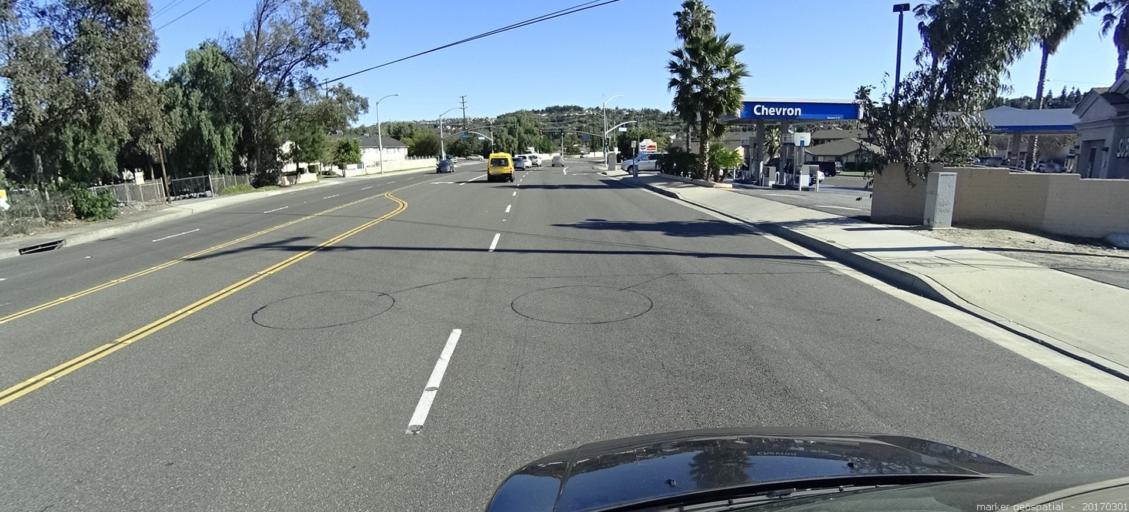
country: US
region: California
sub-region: Orange County
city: Villa Park
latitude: 33.8476
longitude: -117.8359
